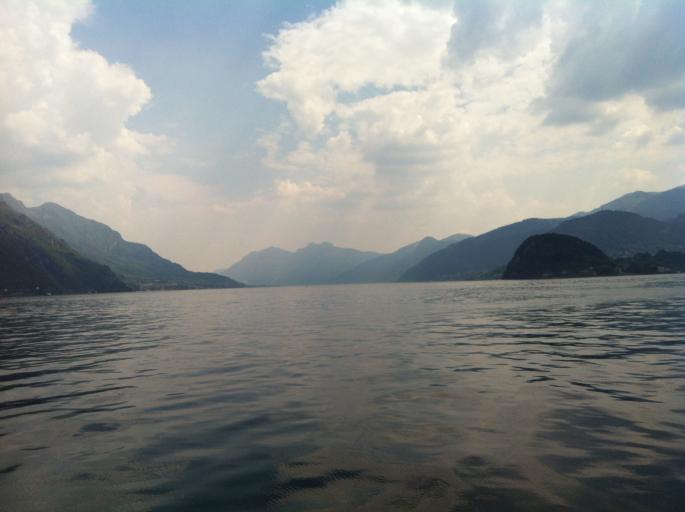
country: IT
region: Lombardy
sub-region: Provincia di Lecco
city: Varenna
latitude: 46.0089
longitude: 9.2676
